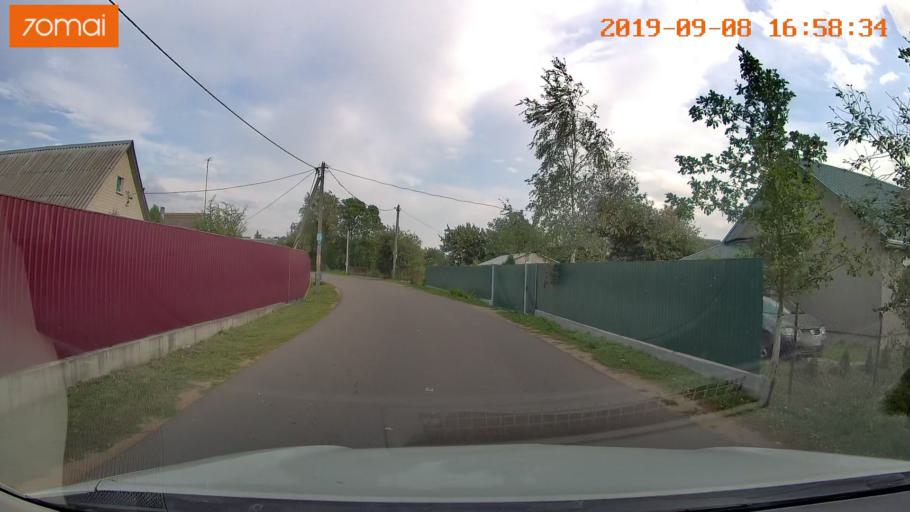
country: BY
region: Grodnenskaya
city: Hrodna
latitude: 53.7259
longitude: 23.9282
